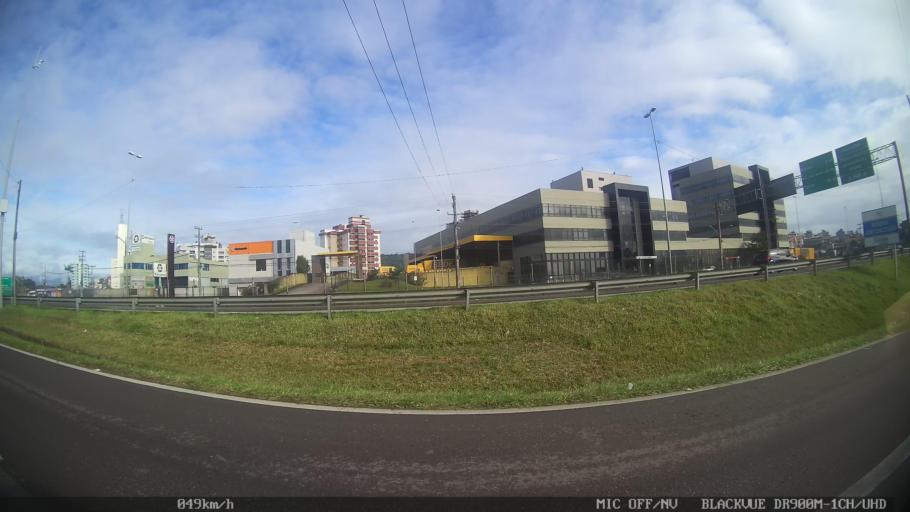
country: BR
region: Santa Catarina
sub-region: Sao Jose
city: Campinas
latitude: -27.5760
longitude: -48.6132
